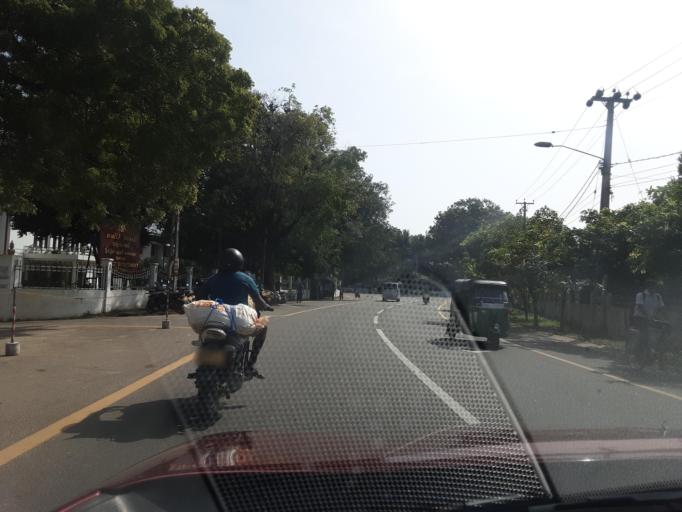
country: LK
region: Northern Province
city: Jaffna
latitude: 9.6606
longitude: 80.0293
